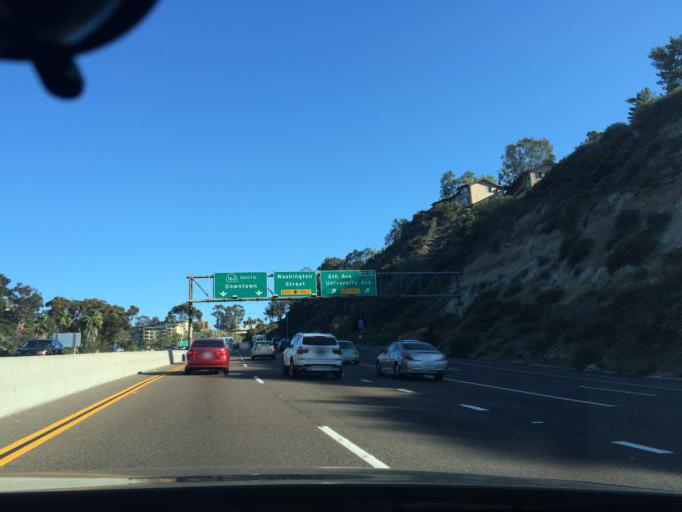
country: US
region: California
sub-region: San Diego County
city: San Diego
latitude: 32.7557
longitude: -117.1589
